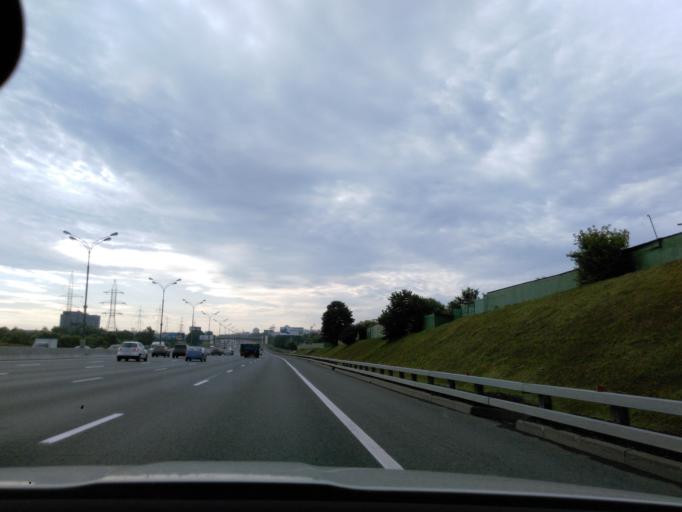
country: RU
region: Moscow
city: Bibirevo
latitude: 55.9018
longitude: 37.6177
